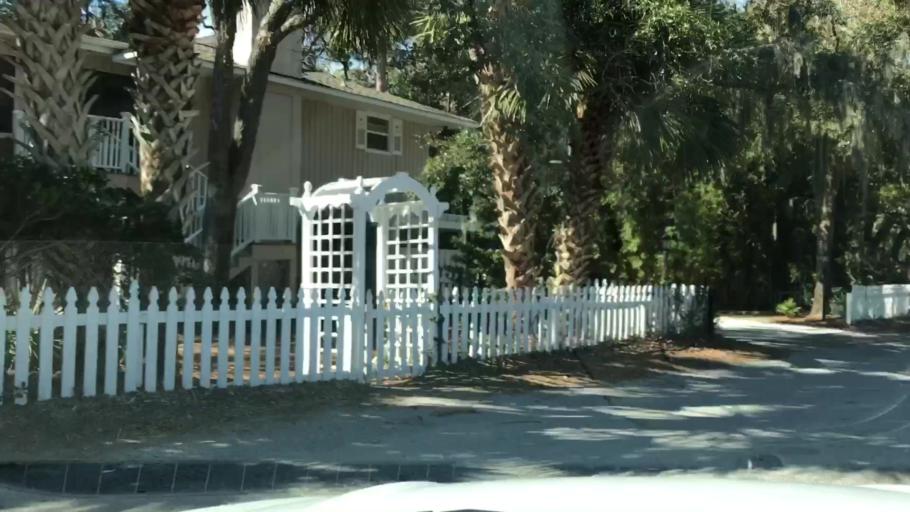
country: US
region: South Carolina
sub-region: Beaufort County
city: Hilton Head Island
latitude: 32.1460
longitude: -80.7423
